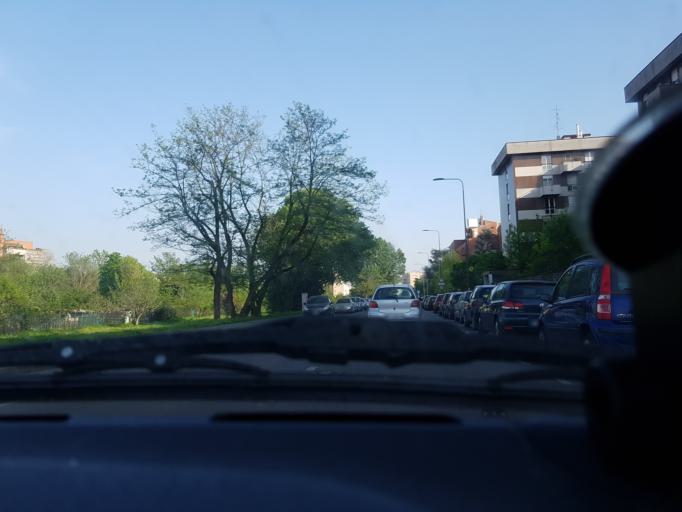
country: IT
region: Lombardy
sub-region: Citta metropolitana di Milano
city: Cesano Boscone
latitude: 45.4573
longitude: 9.0982
